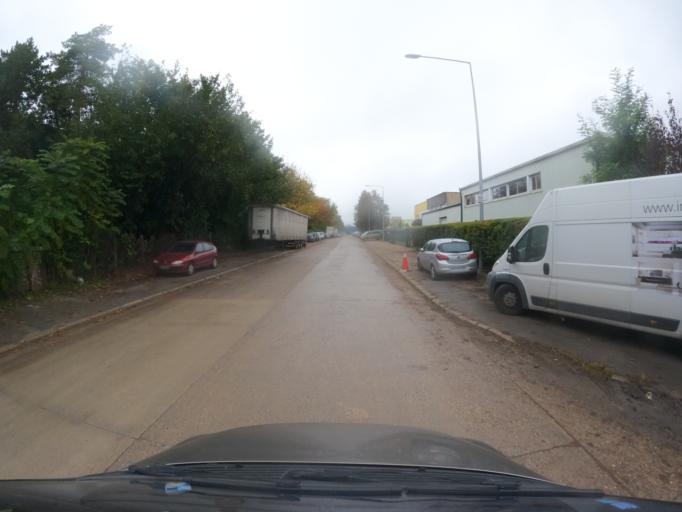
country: FR
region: Ile-de-France
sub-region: Departement du Val-de-Marne
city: Chennevieres-sur-Marne
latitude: 48.7956
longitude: 2.5421
